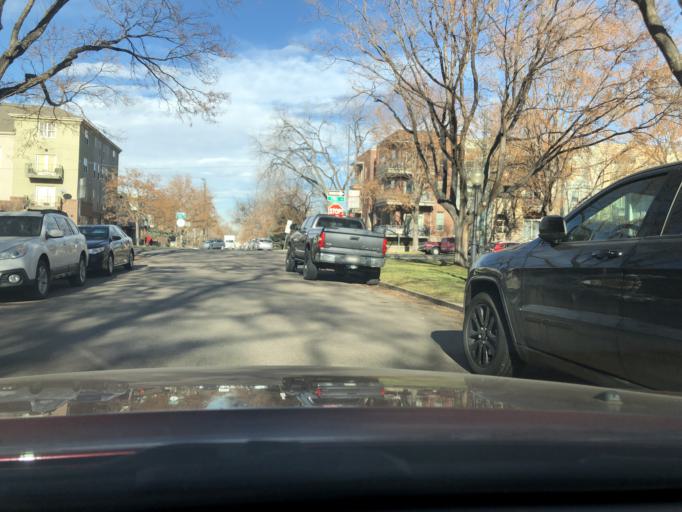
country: US
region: Colorado
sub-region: Denver County
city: Denver
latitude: 39.7428
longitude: -104.9762
